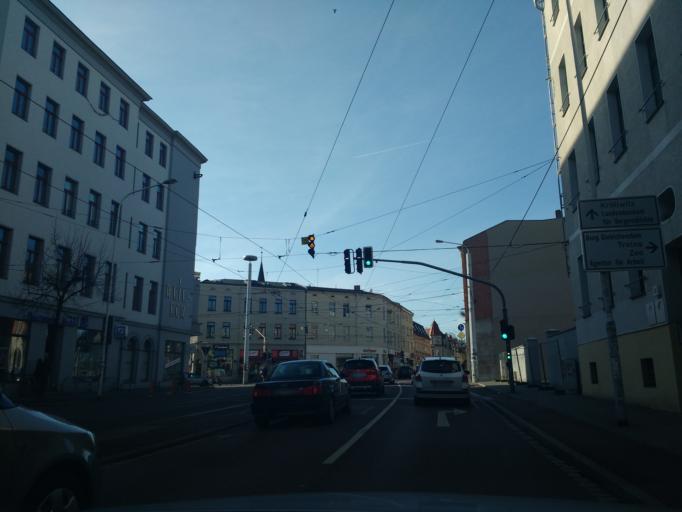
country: DE
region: Saxony-Anhalt
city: Halle (Saale)
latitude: 51.4950
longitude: 11.9671
